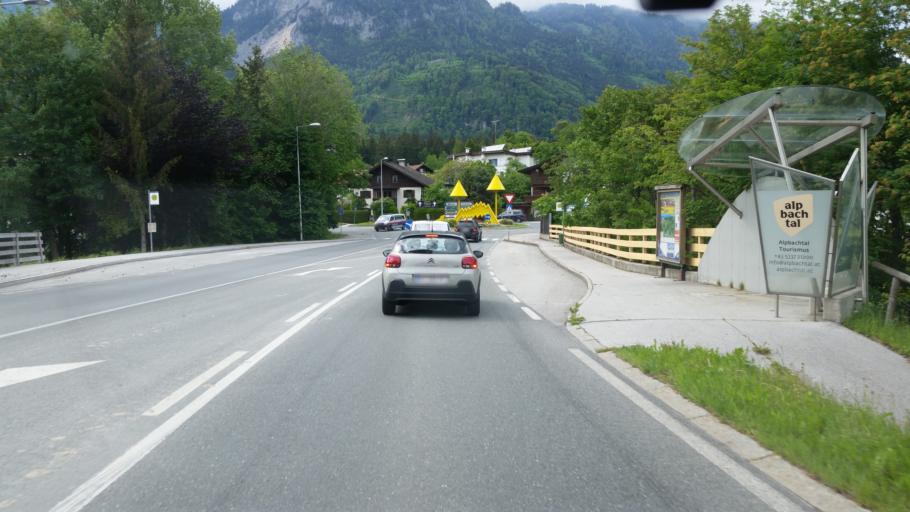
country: AT
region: Tyrol
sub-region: Politischer Bezirk Kufstein
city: Kramsach
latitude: 47.4420
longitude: 11.8774
